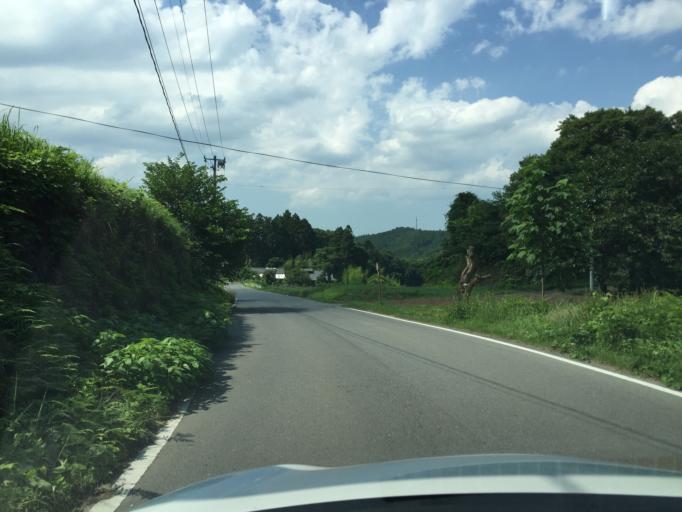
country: JP
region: Ibaraki
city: Kitaibaraki
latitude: 36.9724
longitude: 140.7039
